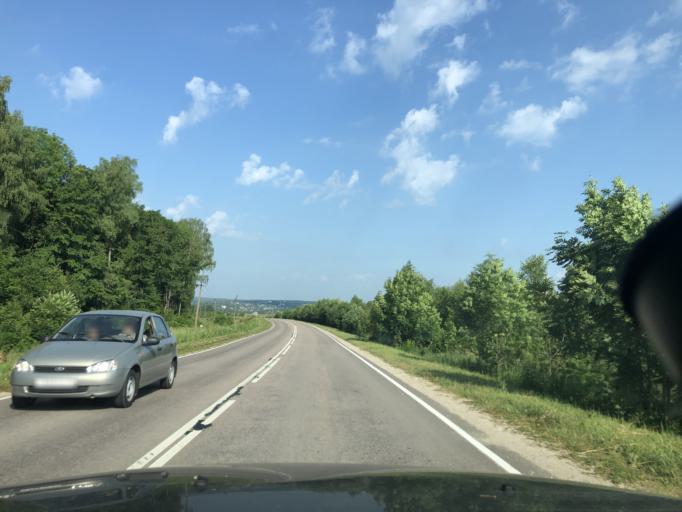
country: RU
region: Tula
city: Dubna
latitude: 54.1400
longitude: 37.0122
